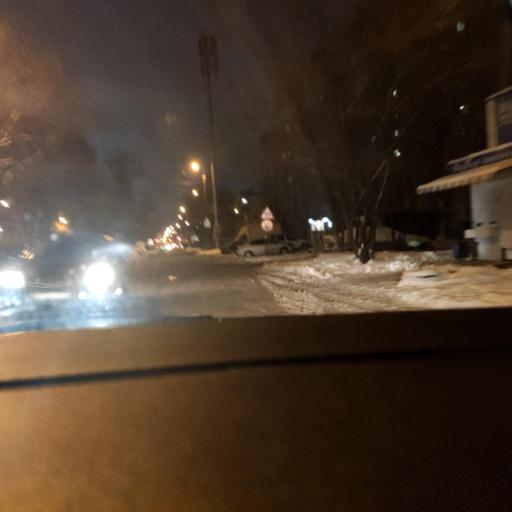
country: RU
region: Voronezj
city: Voronezh
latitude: 51.6402
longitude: 39.2318
